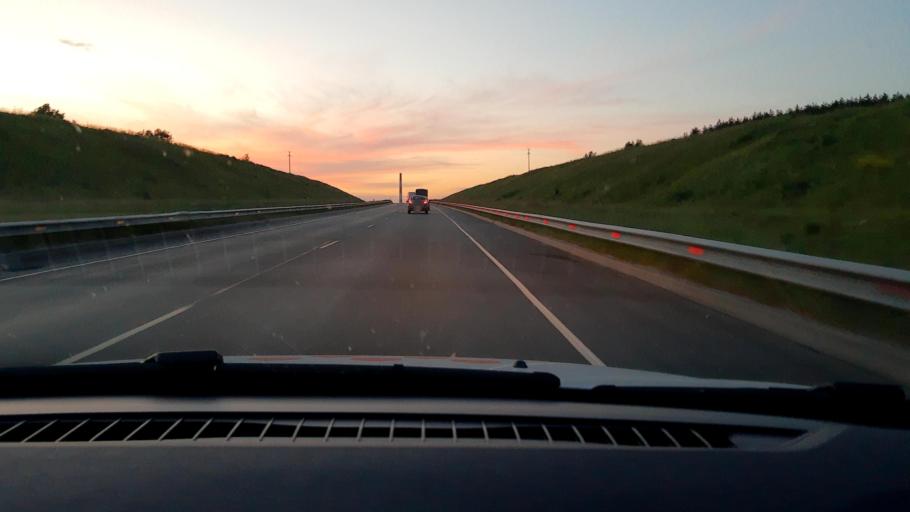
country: RU
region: Nizjnij Novgorod
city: Kstovo
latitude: 56.0814
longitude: 44.1345
